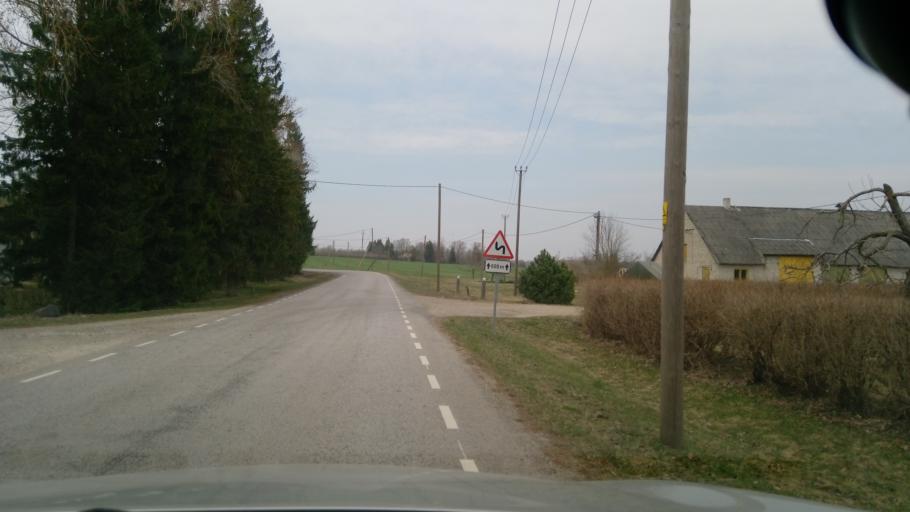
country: EE
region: Jaervamaa
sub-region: Tueri vald
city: Sarevere
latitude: 58.7824
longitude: 25.4792
